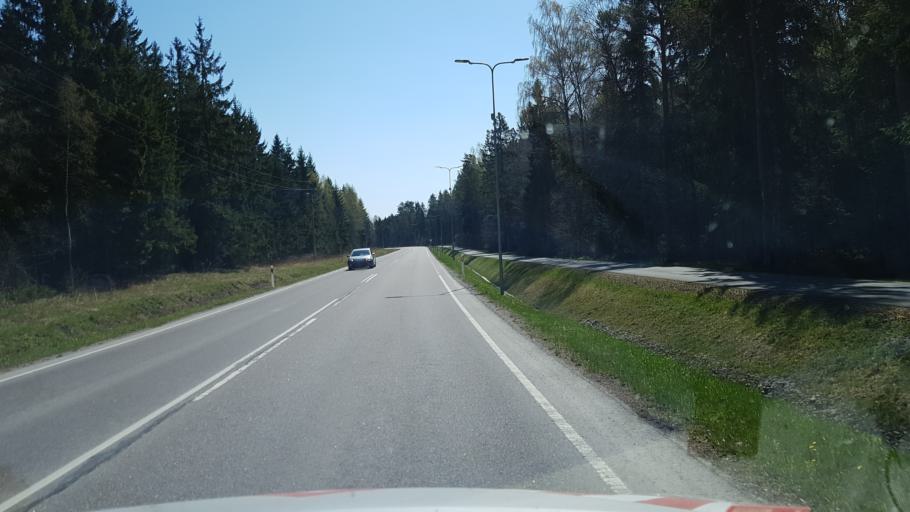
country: EE
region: Harju
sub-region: Viimsi vald
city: Viimsi
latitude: 59.5167
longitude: 24.9003
